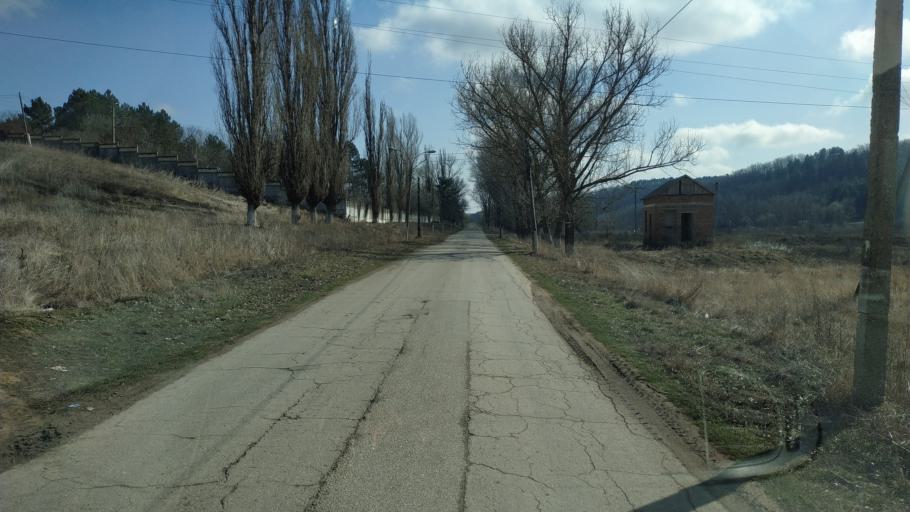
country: MD
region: Hincesti
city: Hincesti
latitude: 46.8711
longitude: 28.6359
